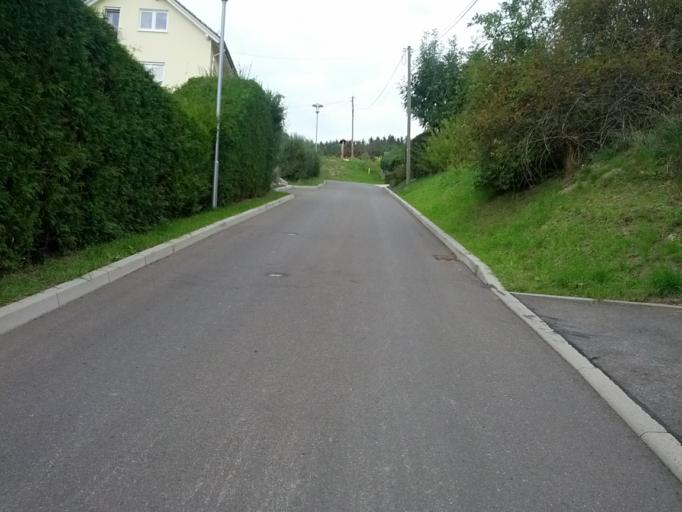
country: DE
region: Thuringia
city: Thal
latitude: 50.9407
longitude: 10.3980
